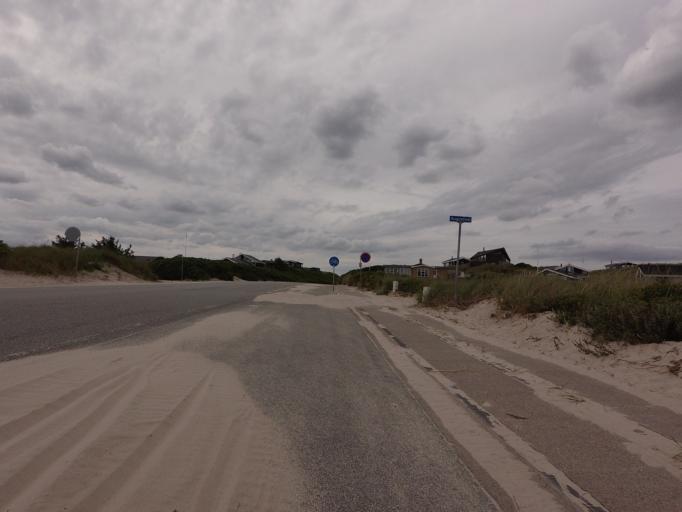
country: DK
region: North Denmark
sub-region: Jammerbugt Kommune
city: Pandrup
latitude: 57.3621
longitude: 9.7035
